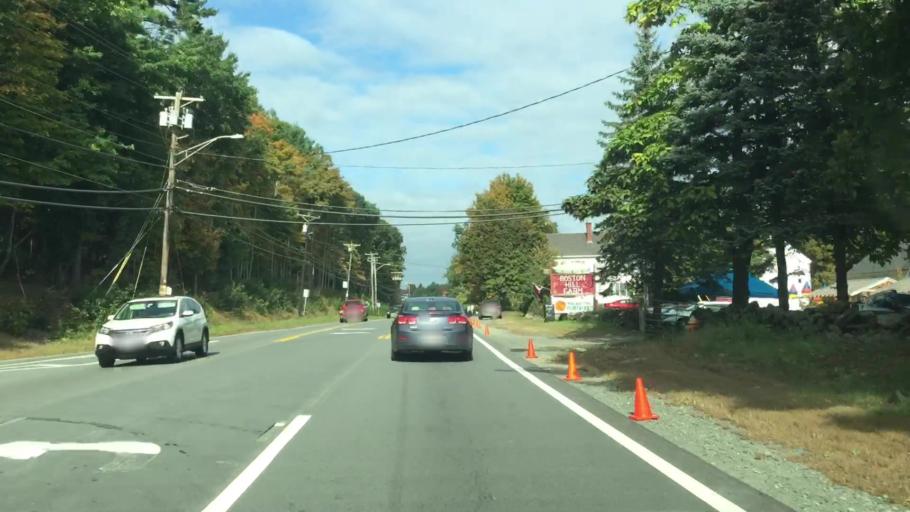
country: US
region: Massachusetts
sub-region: Essex County
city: Andover
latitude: 42.6457
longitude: -71.0886
